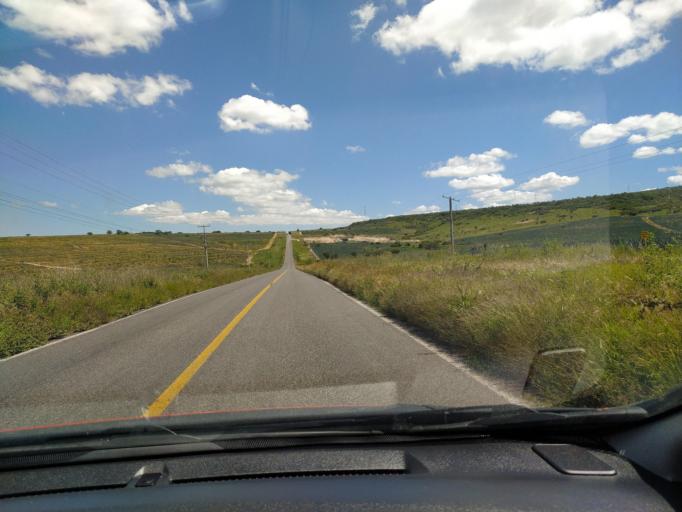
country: MX
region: Jalisco
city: San Diego de Alejandria
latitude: 21.0247
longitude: -101.9375
